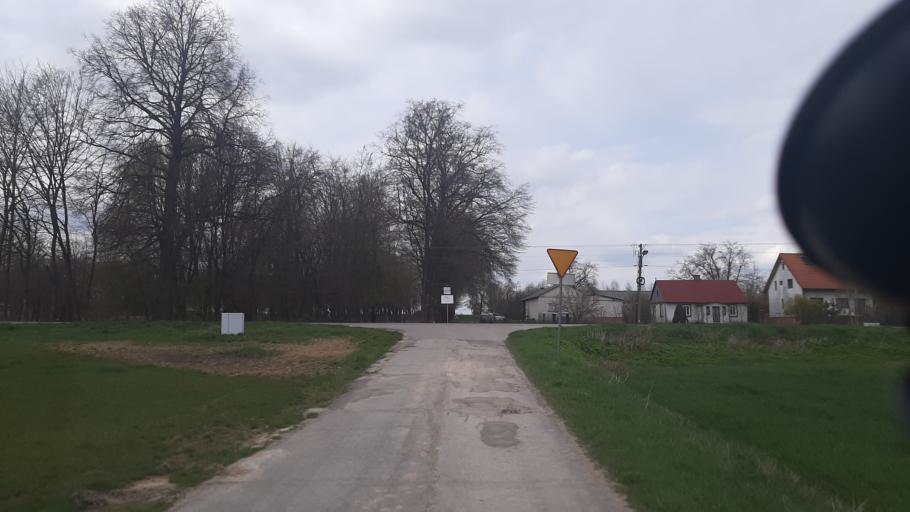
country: PL
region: Lublin Voivodeship
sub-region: Powiat lubelski
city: Jastkow
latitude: 51.3594
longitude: 22.4314
